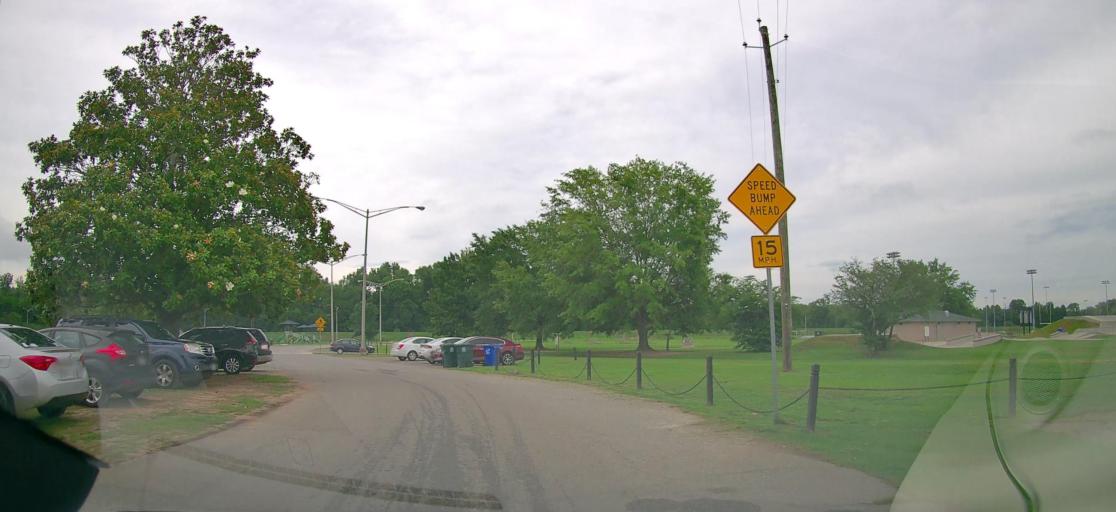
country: US
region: Georgia
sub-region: Bibb County
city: Macon
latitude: 32.8318
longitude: -83.6147
